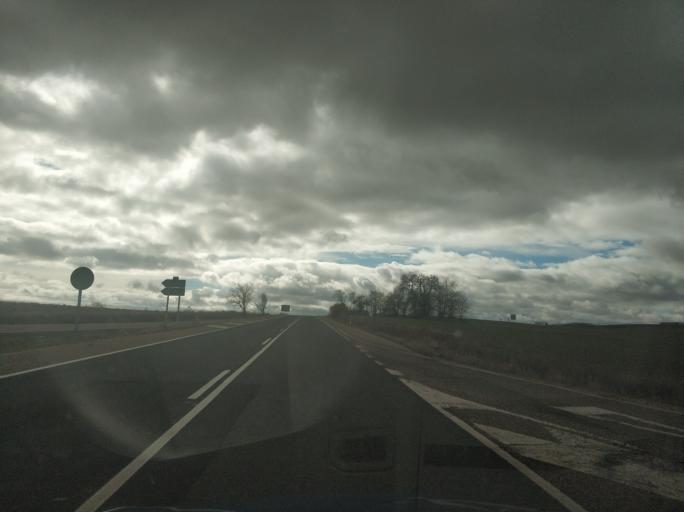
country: ES
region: Castille and Leon
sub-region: Provincia de Zamora
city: Castrillo de la Guarena
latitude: 41.2242
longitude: -5.3143
